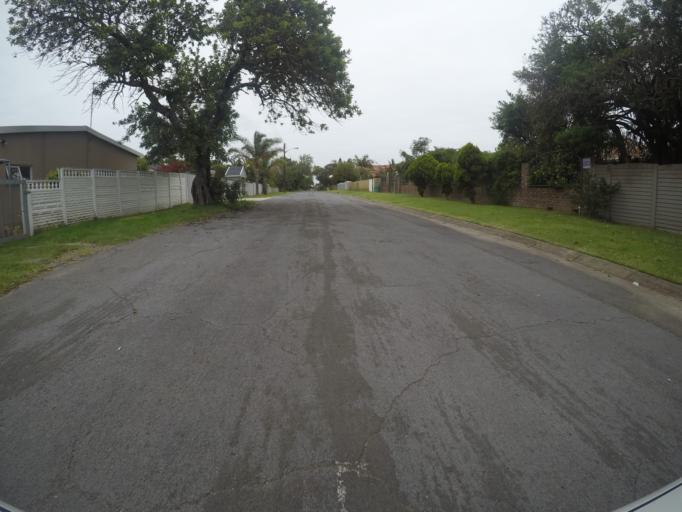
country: ZA
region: Eastern Cape
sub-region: Buffalo City Metropolitan Municipality
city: East London
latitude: -32.9685
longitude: 27.9376
